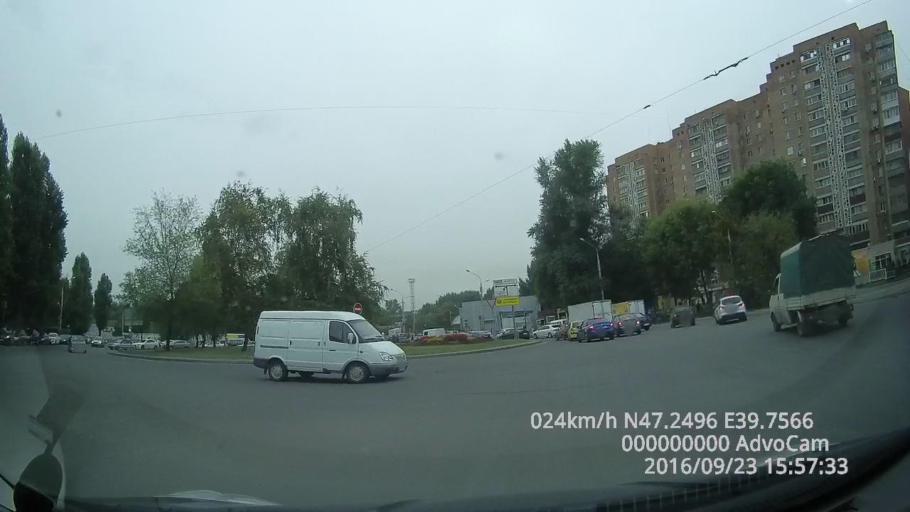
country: RU
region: Rostov
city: Imeni Chkalova
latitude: 47.2495
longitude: 39.7566
